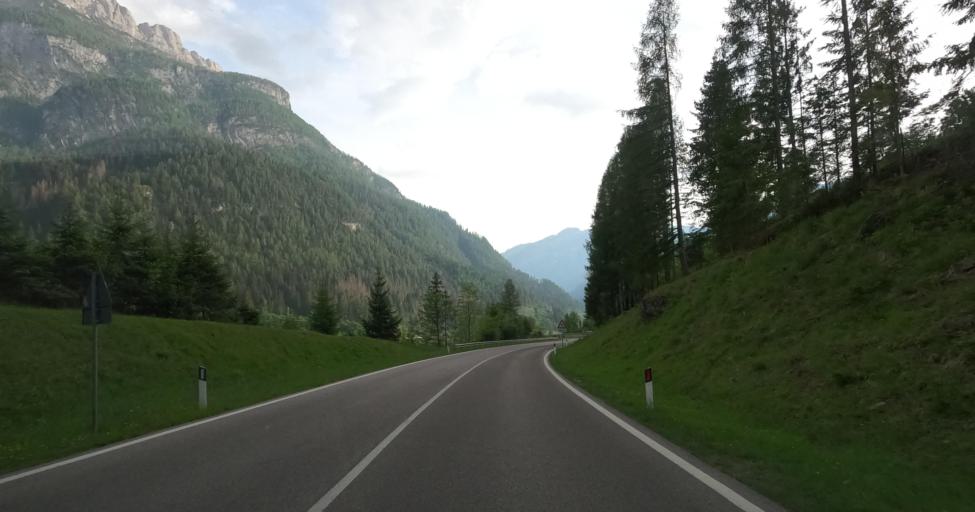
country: IT
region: Veneto
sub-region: Provincia di Belluno
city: Celat-San Tomaso Agordino
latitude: 46.3904
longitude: 11.9979
